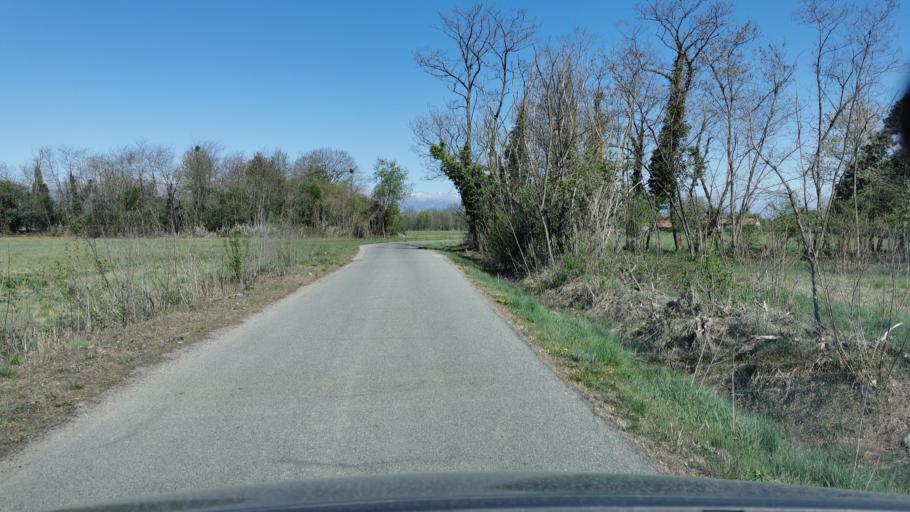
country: IT
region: Piedmont
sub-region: Provincia di Torino
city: Leini
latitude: 45.1977
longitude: 7.6967
